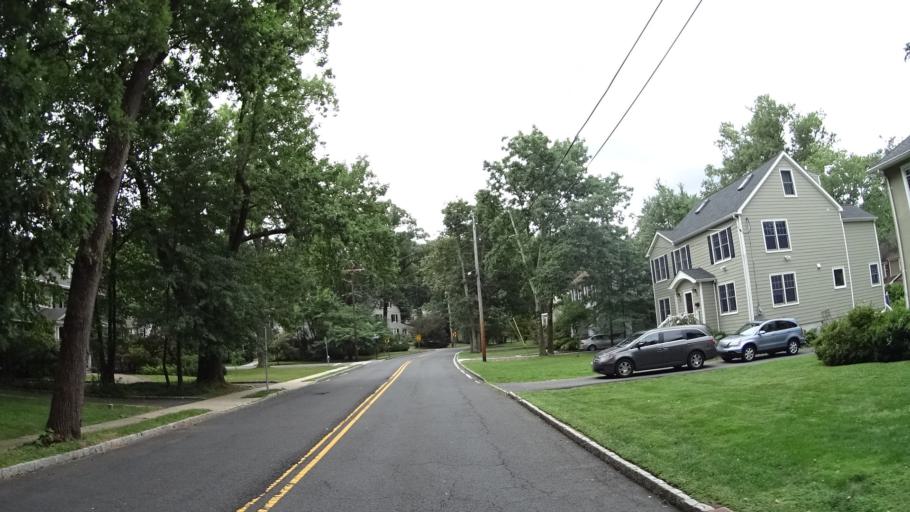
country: US
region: New Jersey
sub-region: Union County
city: Mountainside
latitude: 40.7061
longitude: -74.3623
